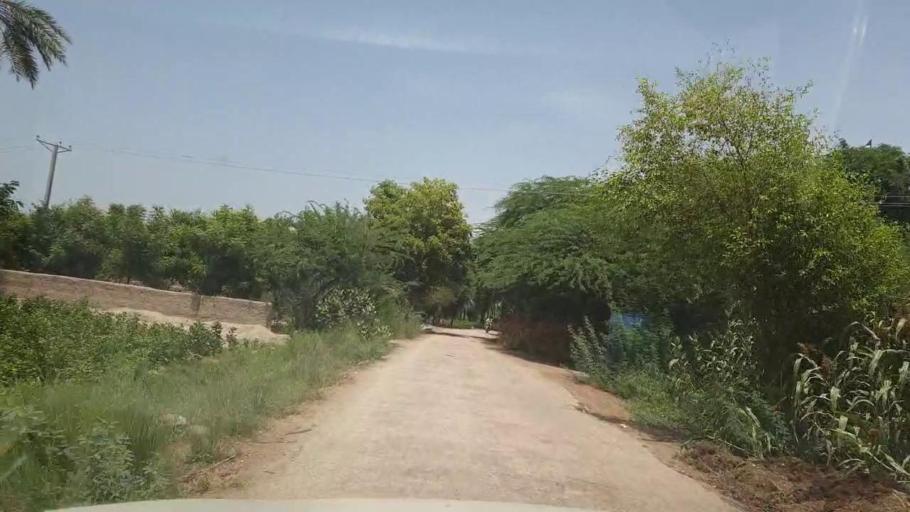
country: PK
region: Sindh
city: Bozdar
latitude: 27.1773
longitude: 68.6302
